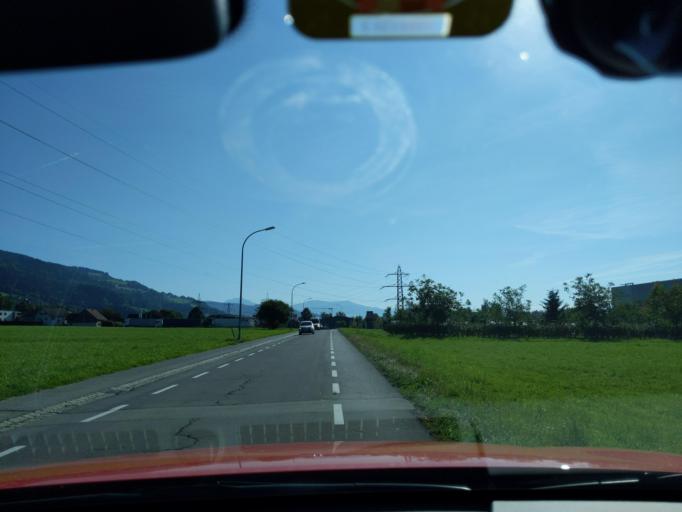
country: AT
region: Vorarlberg
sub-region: Politischer Bezirk Bregenz
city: Horbranz
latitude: 47.5454
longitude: 9.7513
